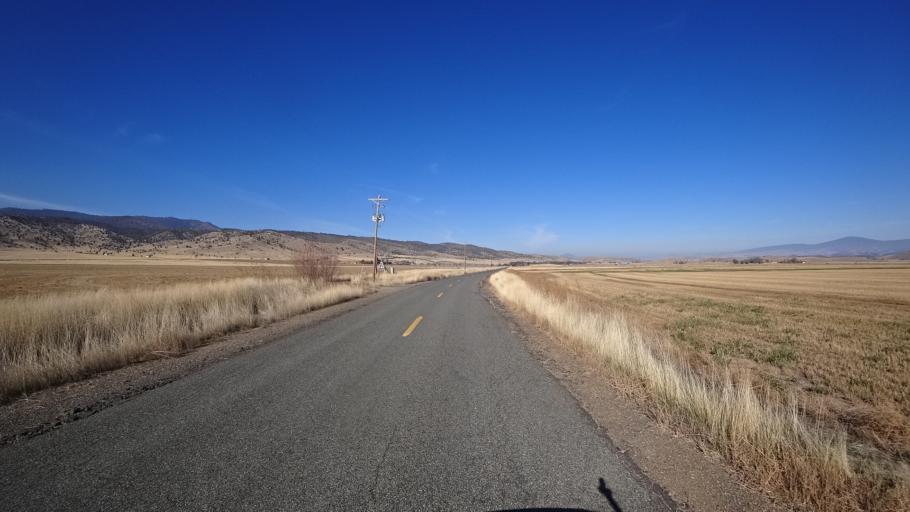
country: US
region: California
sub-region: Siskiyou County
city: Montague
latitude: 41.5638
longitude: -122.5488
